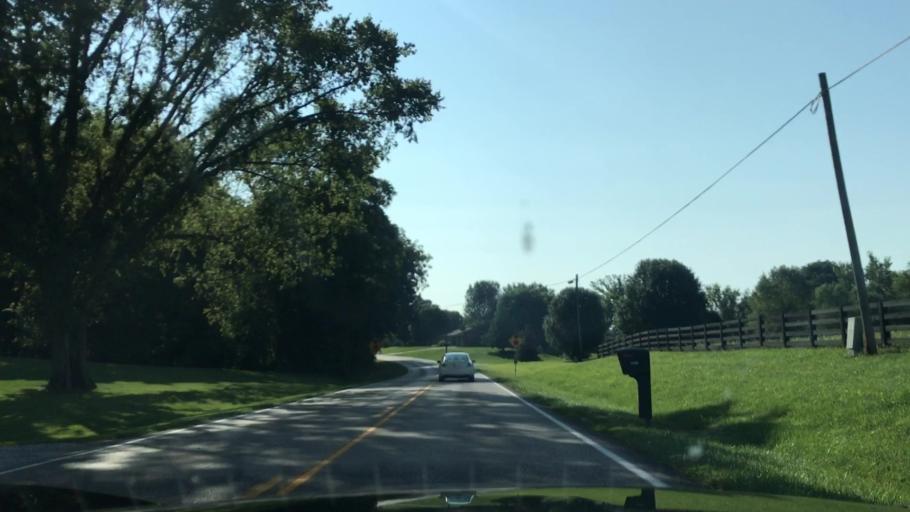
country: US
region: Kentucky
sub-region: Hart County
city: Horse Cave
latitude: 37.1673
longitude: -85.8455
